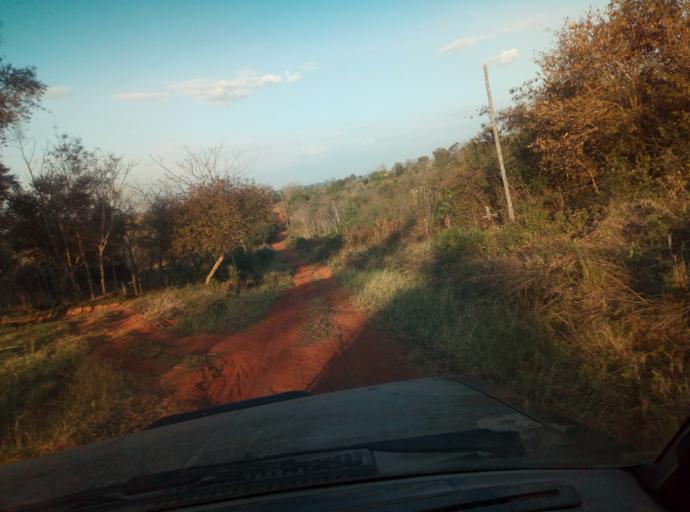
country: PY
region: Caaguazu
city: Doctor Cecilio Baez
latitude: -25.1530
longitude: -56.2397
